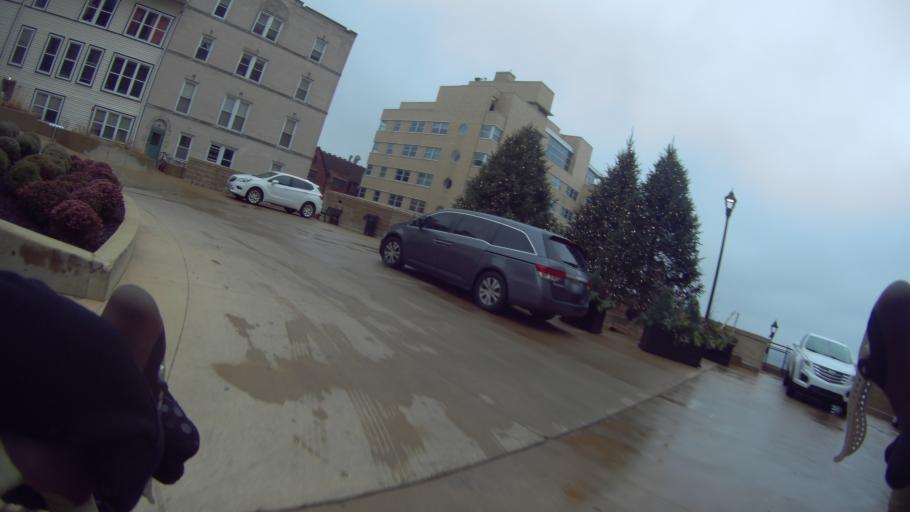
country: US
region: Wisconsin
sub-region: Dane County
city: Madison
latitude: 43.0791
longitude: -89.3897
